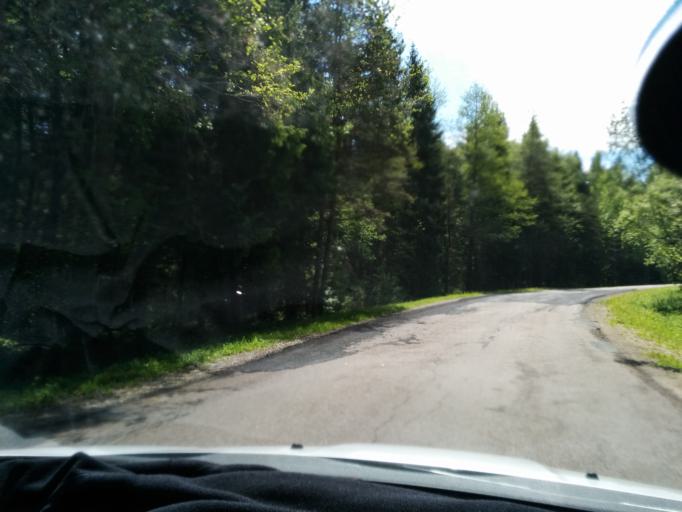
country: EE
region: Harju
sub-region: Loksa linn
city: Loksa
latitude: 59.5903
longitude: 25.9091
